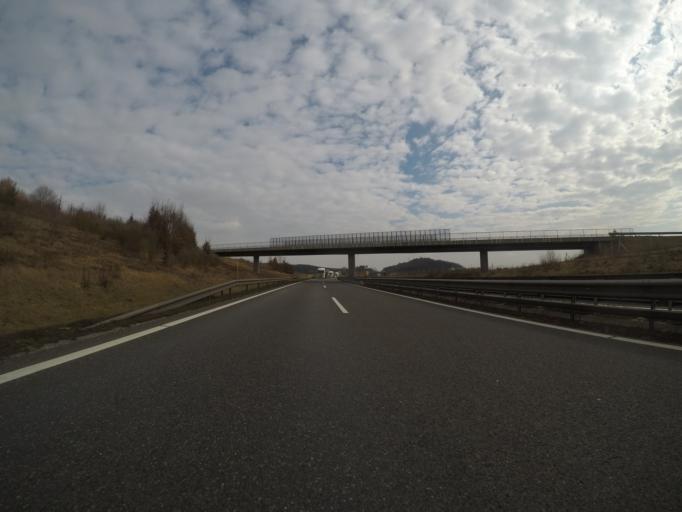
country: SI
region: Sveti Jurij
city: Sveti Jurij ob Scavnici
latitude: 46.5860
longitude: 16.0351
